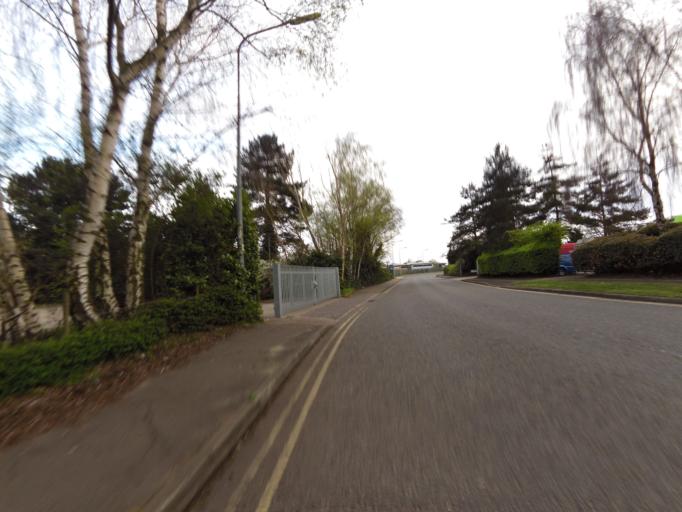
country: GB
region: England
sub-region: Suffolk
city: Kesgrave
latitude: 52.0294
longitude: 1.2158
